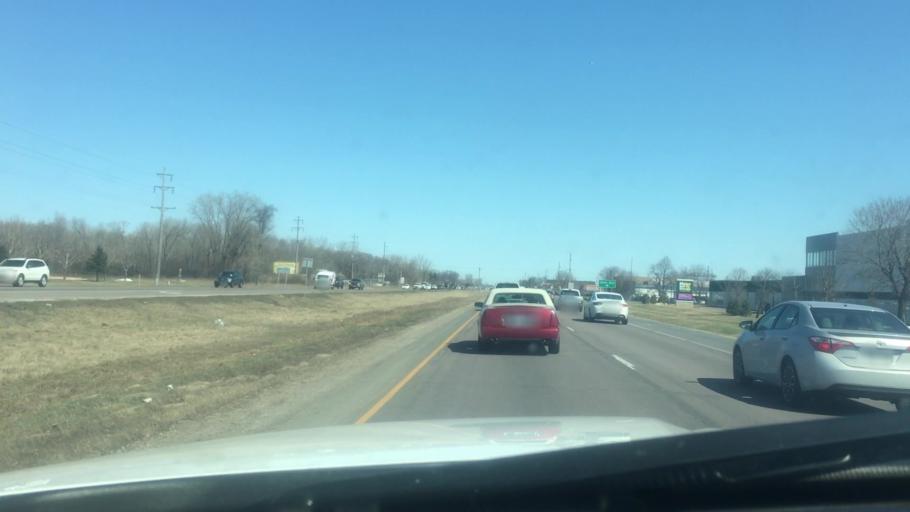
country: US
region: Minnesota
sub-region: Anoka County
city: Blaine
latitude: 45.1503
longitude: -93.2351
